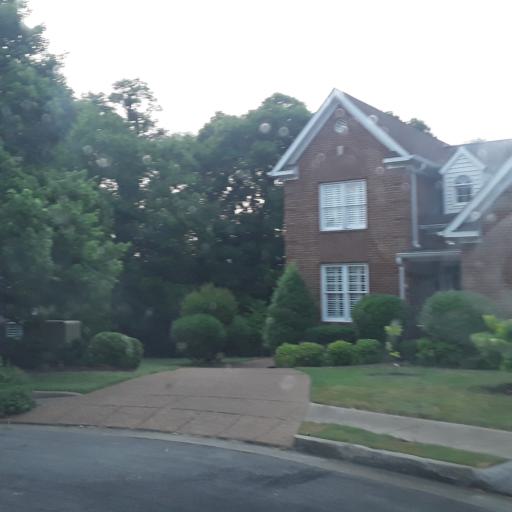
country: US
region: Tennessee
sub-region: Williamson County
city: Brentwood
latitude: 36.0484
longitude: -86.7718
